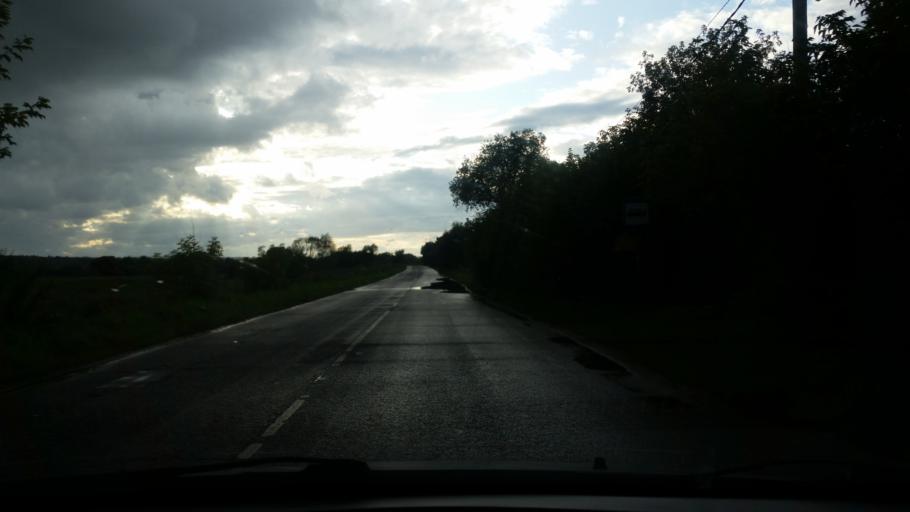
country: RU
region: Moskovskaya
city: Bol'shoye Gryzlovo
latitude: 54.8714
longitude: 37.8321
